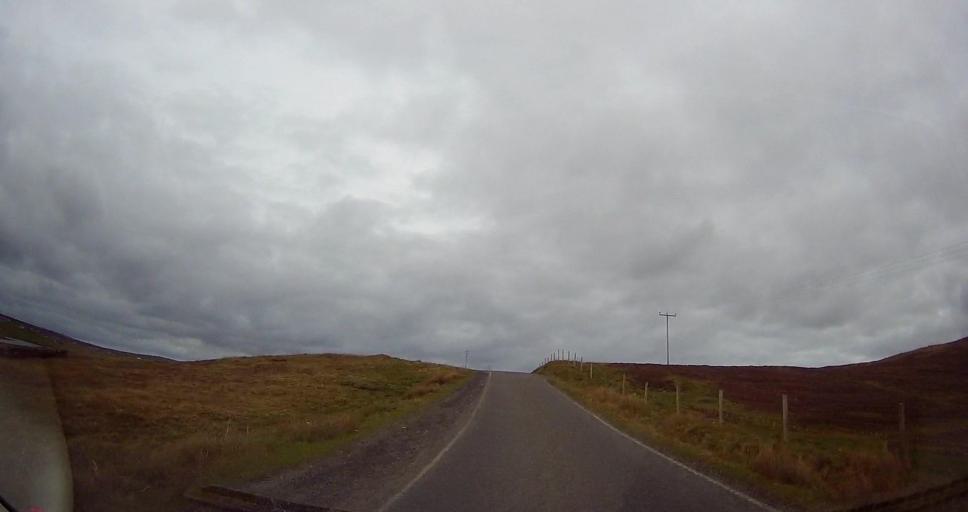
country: GB
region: Scotland
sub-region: Shetland Islands
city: Shetland
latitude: 60.6041
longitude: -1.0910
